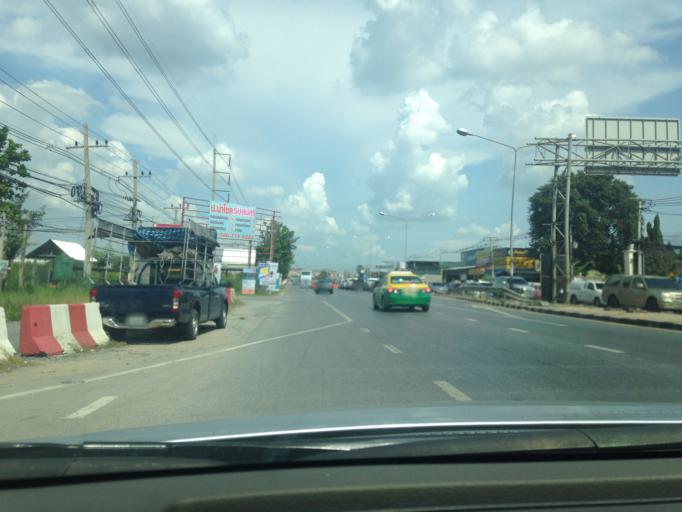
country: TH
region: Phra Nakhon Si Ayutthaya
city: Ban Bang Kadi Pathum Thani
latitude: 14.0053
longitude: 100.5575
